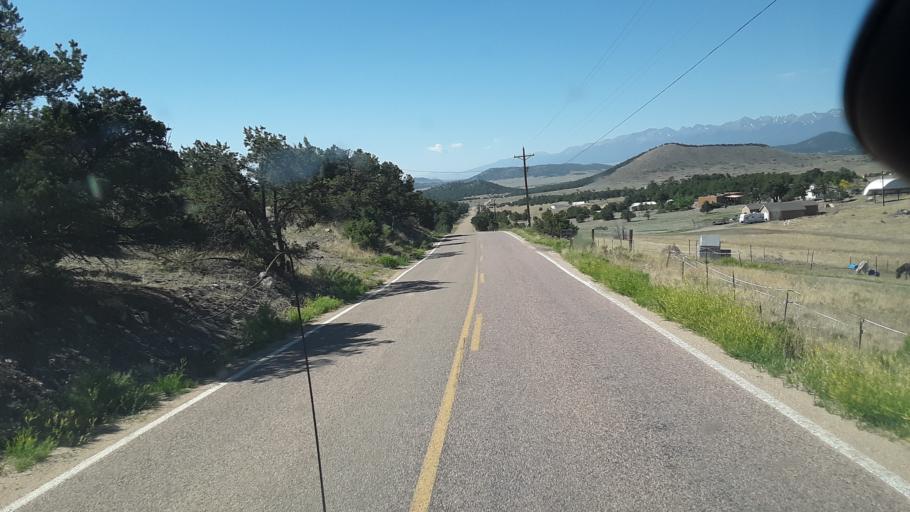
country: US
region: Colorado
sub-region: Custer County
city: Westcliffe
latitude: 38.3231
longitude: -105.4877
